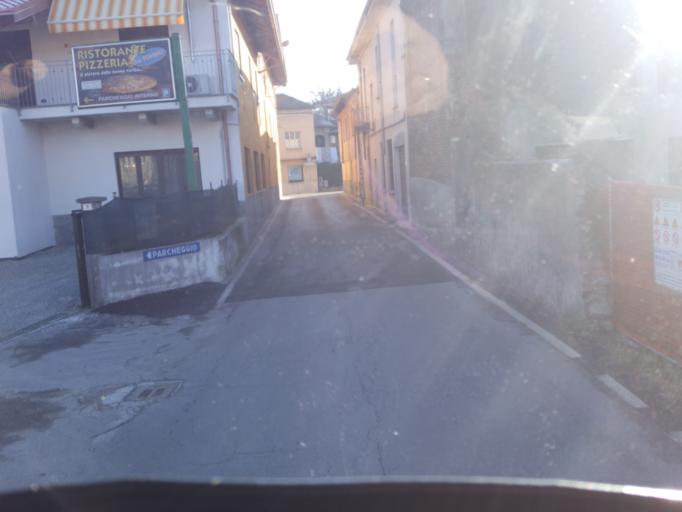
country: IT
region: Piedmont
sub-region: Provincia di Novara
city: Castelletto Sopra Ticino
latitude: 45.7141
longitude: 8.6390
